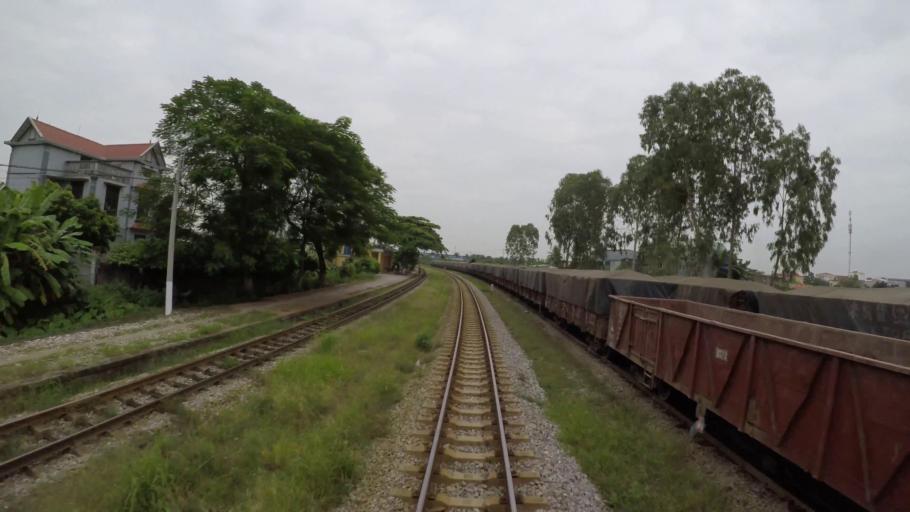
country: VN
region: Hai Phong
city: An Duong
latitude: 20.9065
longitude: 106.5742
